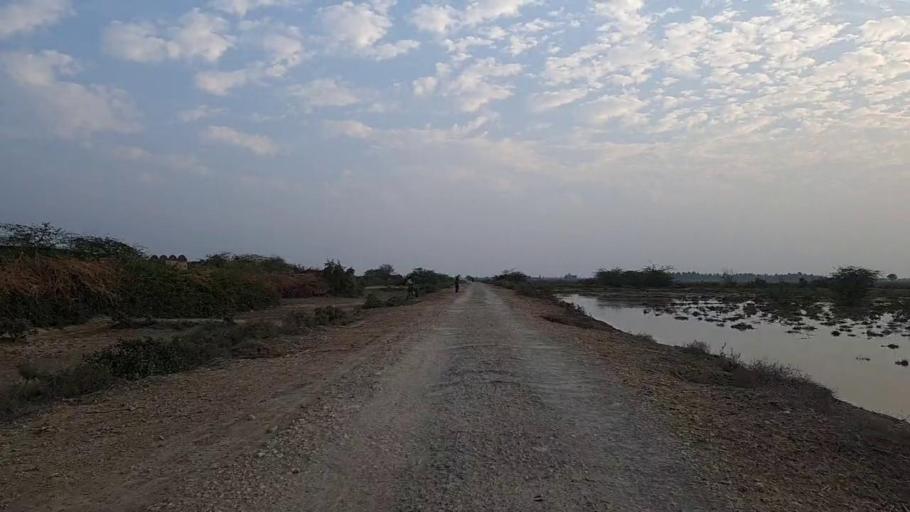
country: PK
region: Sindh
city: Pithoro
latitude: 25.4530
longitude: 69.3452
